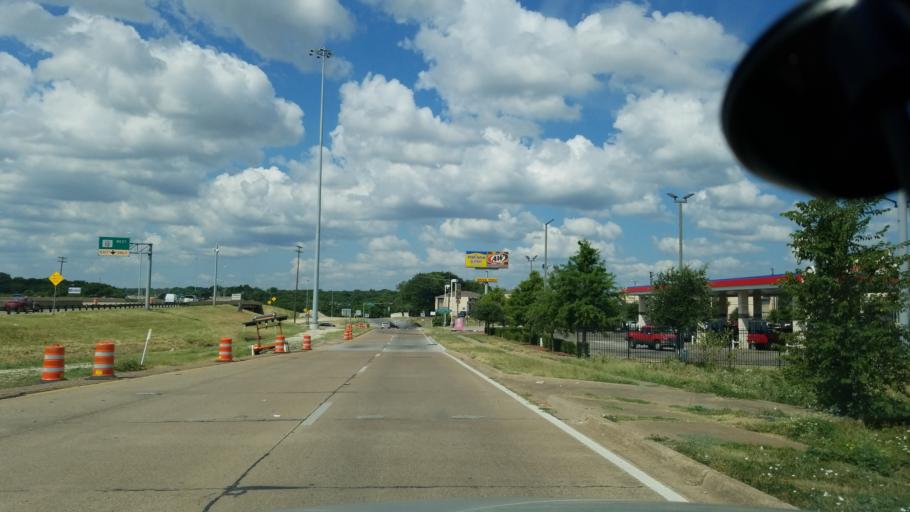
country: US
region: Texas
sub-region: Dallas County
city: Cockrell Hill
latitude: 32.6998
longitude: -96.8384
